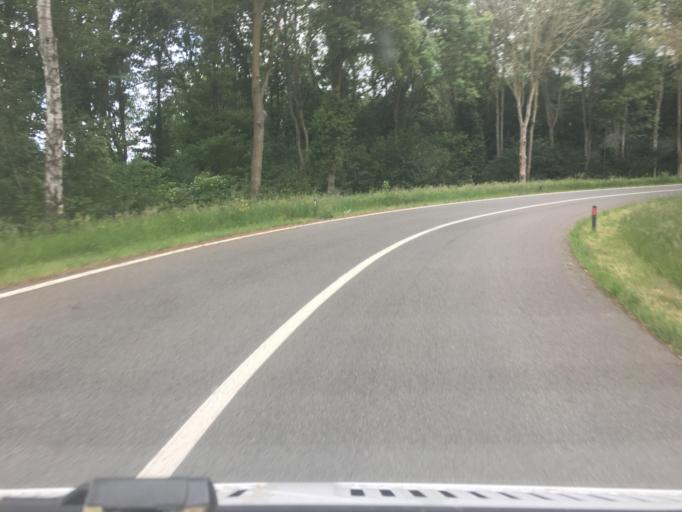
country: NL
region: Gelderland
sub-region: Gemeente Doesburg
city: Doesburg
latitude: 51.9973
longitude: 6.1391
